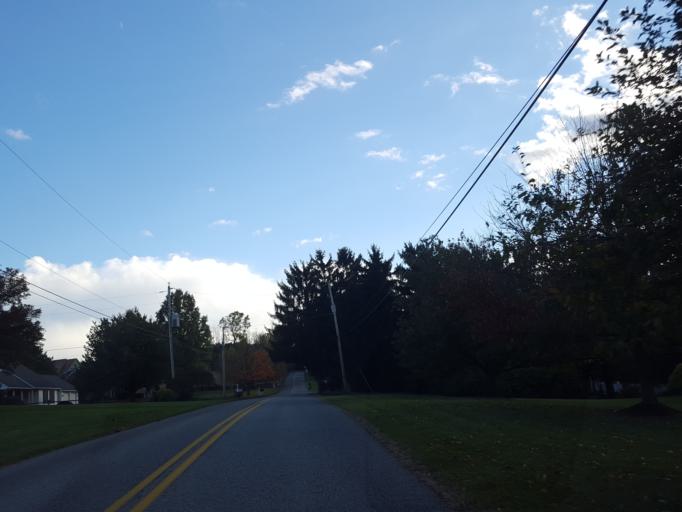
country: US
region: Pennsylvania
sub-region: York County
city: Spry
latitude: 39.9270
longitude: -76.6725
